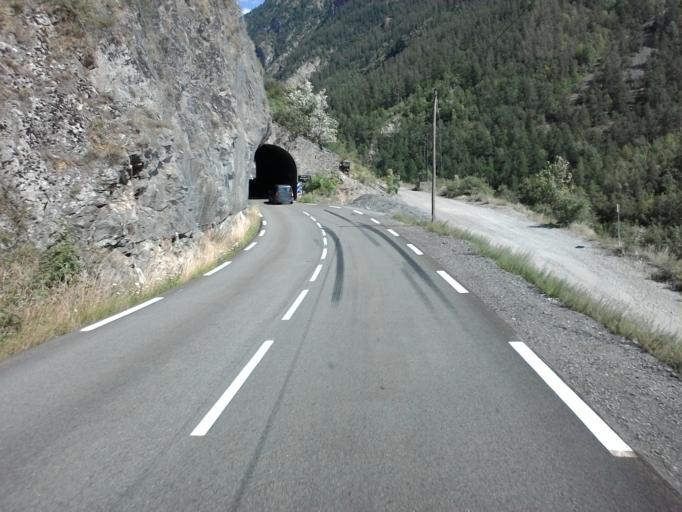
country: FR
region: Rhone-Alpes
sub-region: Departement de l'Isere
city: Mont-de-Lans
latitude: 45.0405
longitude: 6.1736
